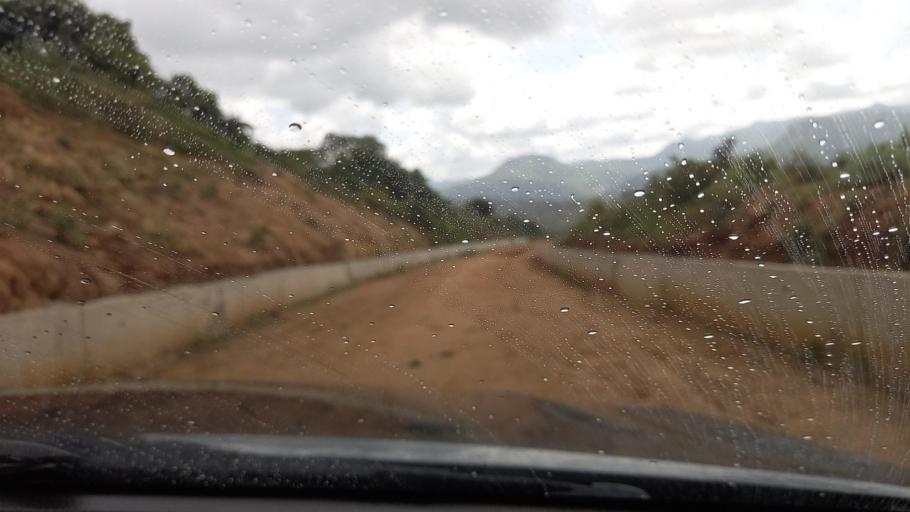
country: ET
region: Southern Nations, Nationalities, and People's Region
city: Mizan Teferi
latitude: 6.1751
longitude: 35.7114
